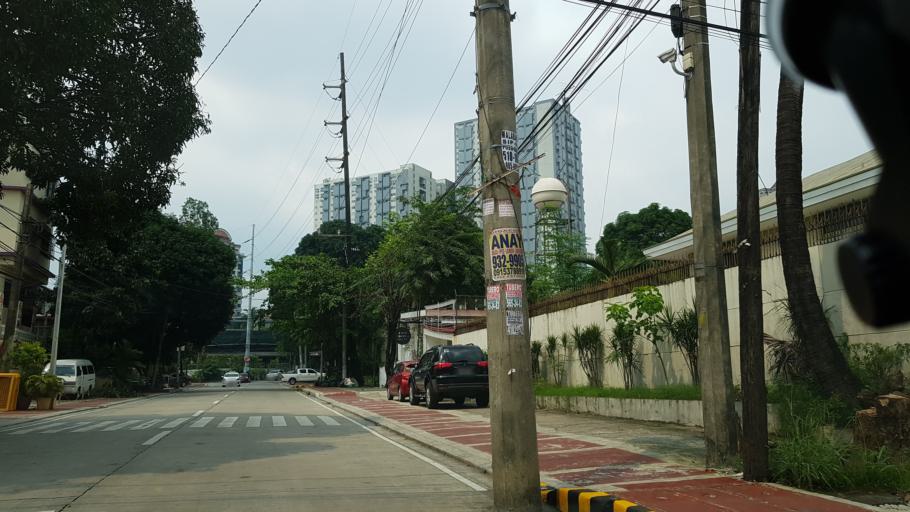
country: PH
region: Calabarzon
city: Del Monte
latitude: 14.6335
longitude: 121.0262
